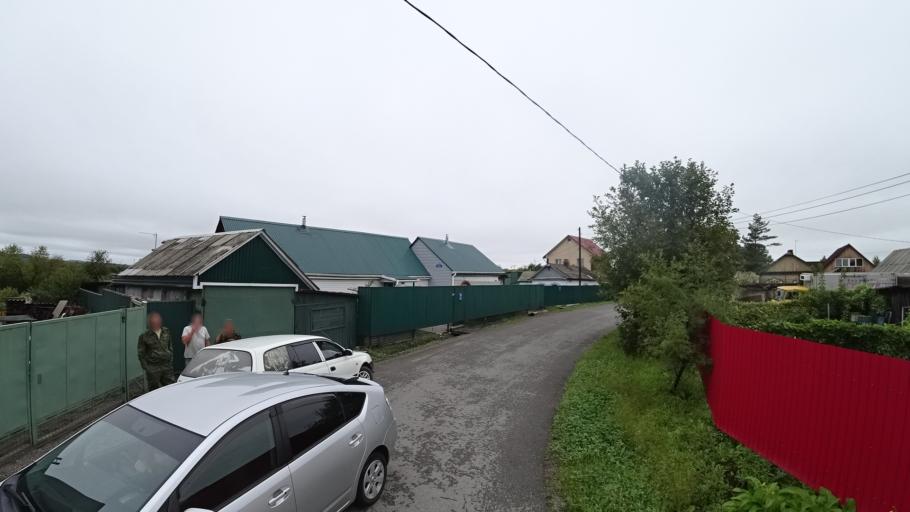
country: RU
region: Primorskiy
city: Monastyrishche
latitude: 44.2028
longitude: 132.4413
